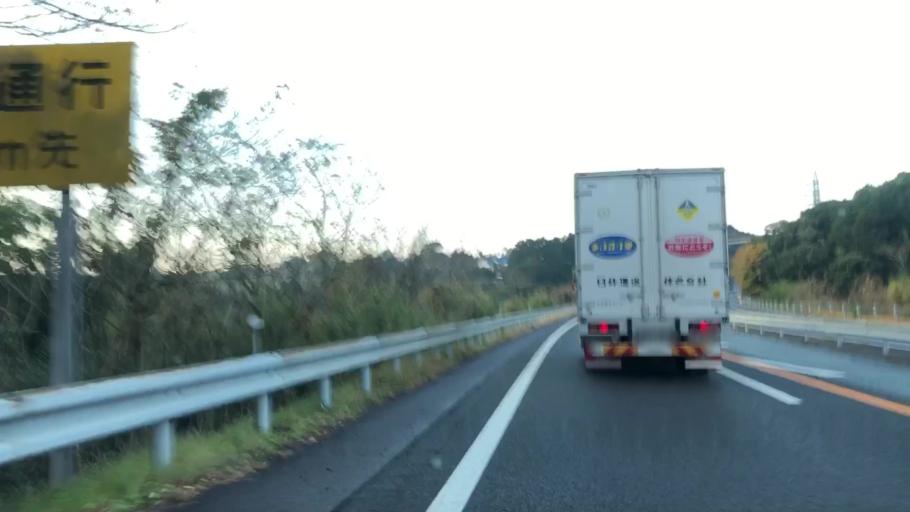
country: JP
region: Nagasaki
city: Sasebo
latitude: 33.1535
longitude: 129.8117
